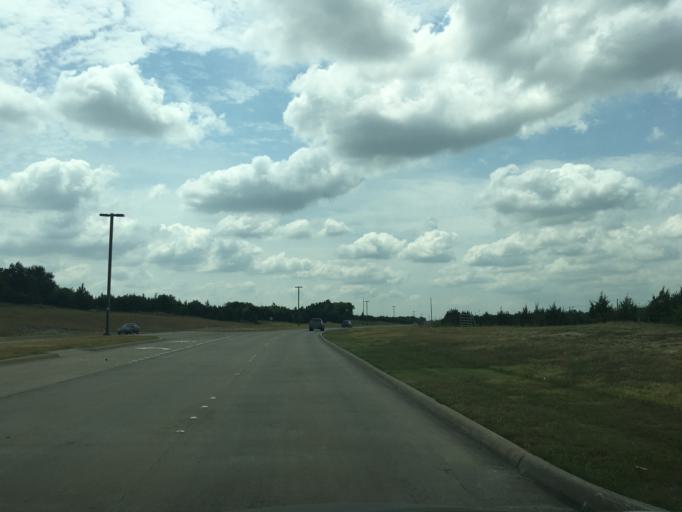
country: US
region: Texas
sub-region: Rockwall County
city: Rockwall
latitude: 32.9330
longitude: -96.4387
